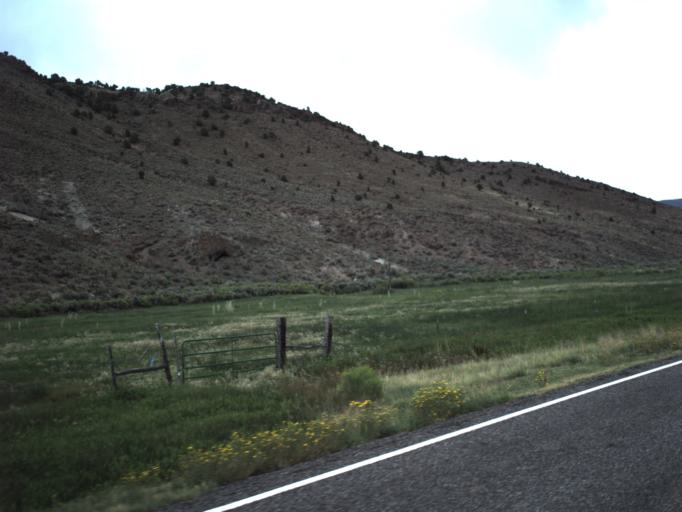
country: US
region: Utah
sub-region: Piute County
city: Junction
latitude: 38.1688
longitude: -112.0428
